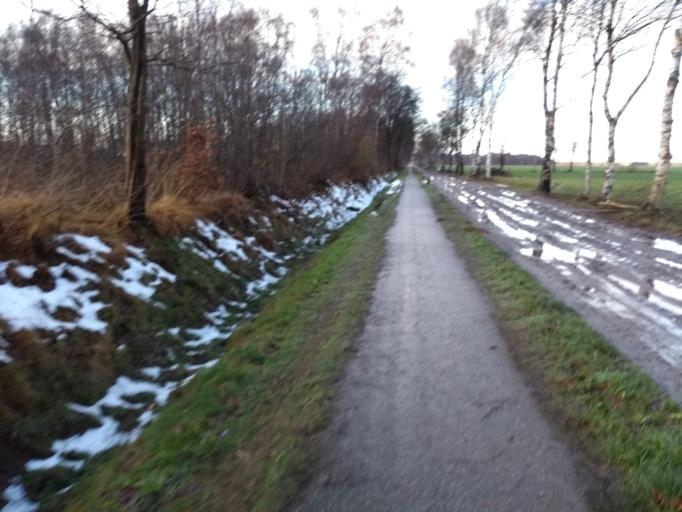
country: NL
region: Overijssel
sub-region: Gemeente Wierden
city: Wierden
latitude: 52.3658
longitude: 6.5224
